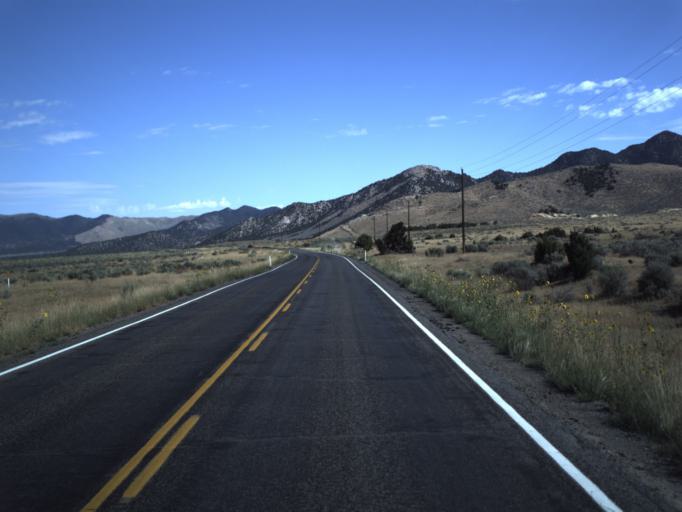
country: US
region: Utah
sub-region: Juab County
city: Mona
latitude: 39.8991
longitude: -112.1380
